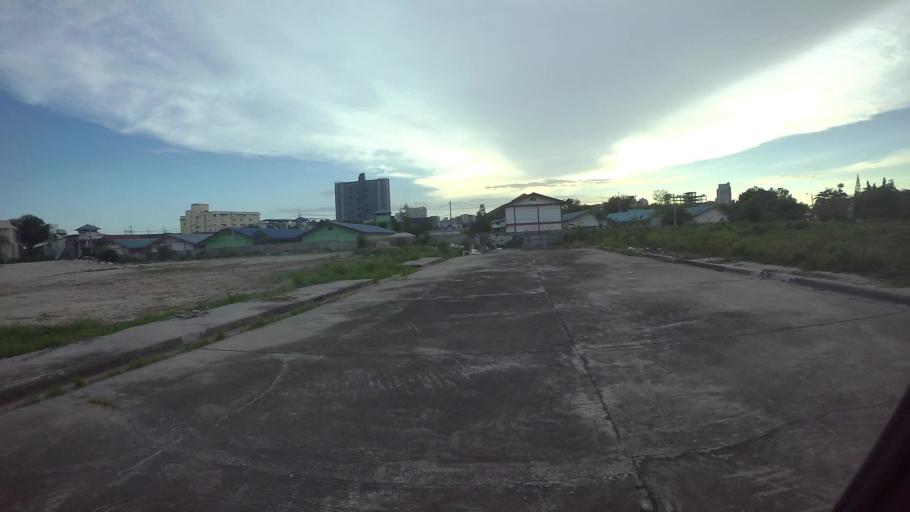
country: TH
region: Chon Buri
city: Phatthaya
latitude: 12.9096
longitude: 100.8844
